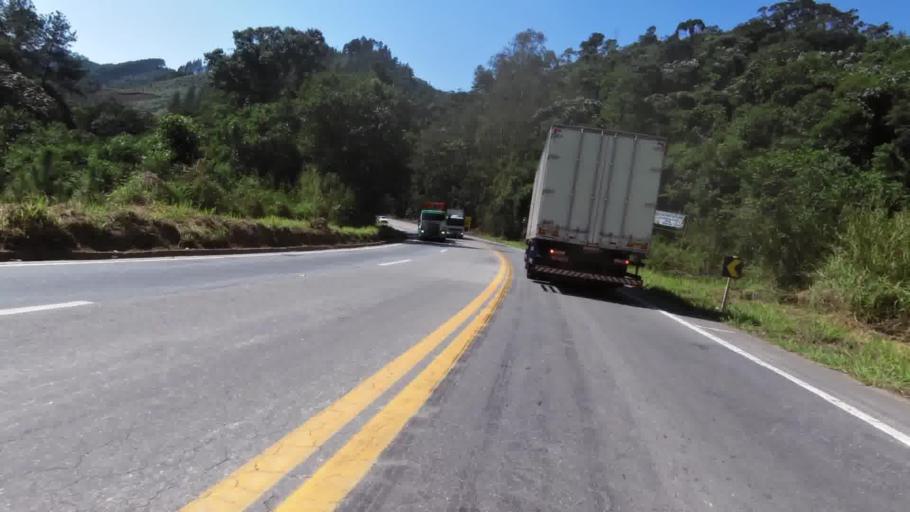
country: BR
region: Espirito Santo
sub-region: Marechal Floriano
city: Marechal Floriano
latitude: -20.4168
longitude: -40.8651
